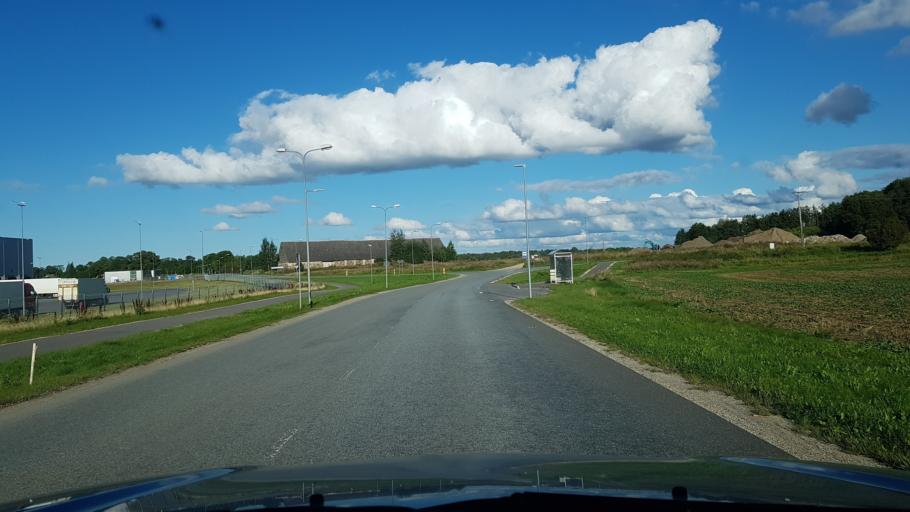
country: EE
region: Harju
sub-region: Kiili vald
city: Kiili
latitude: 59.3337
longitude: 24.8313
